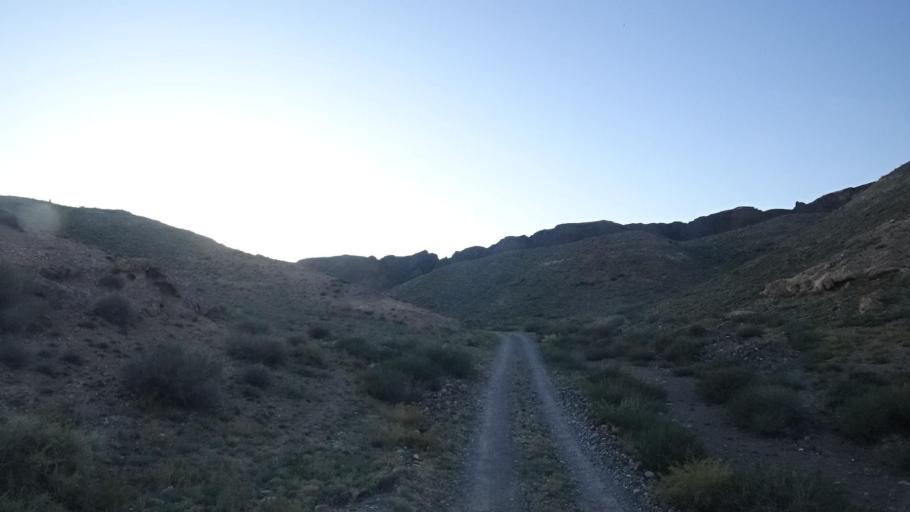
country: KZ
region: Almaty Oblysy
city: Kegen
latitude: 43.2724
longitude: 78.9749
